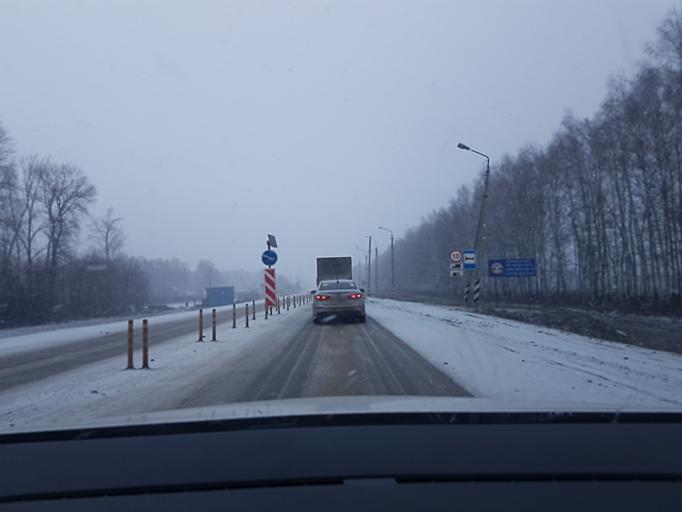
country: RU
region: Tambov
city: Pervomayskiy
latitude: 53.3101
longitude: 40.2203
